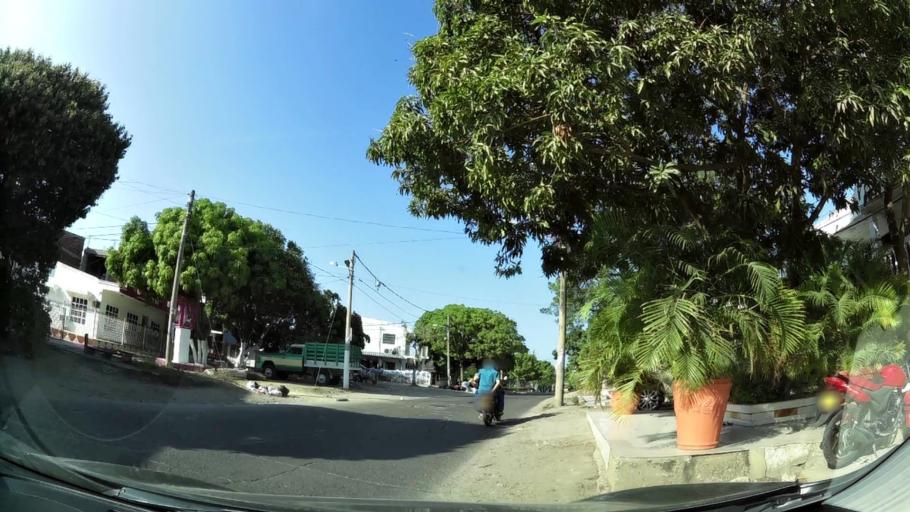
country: CO
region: Bolivar
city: Cartagena
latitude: 10.3815
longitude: -75.4838
